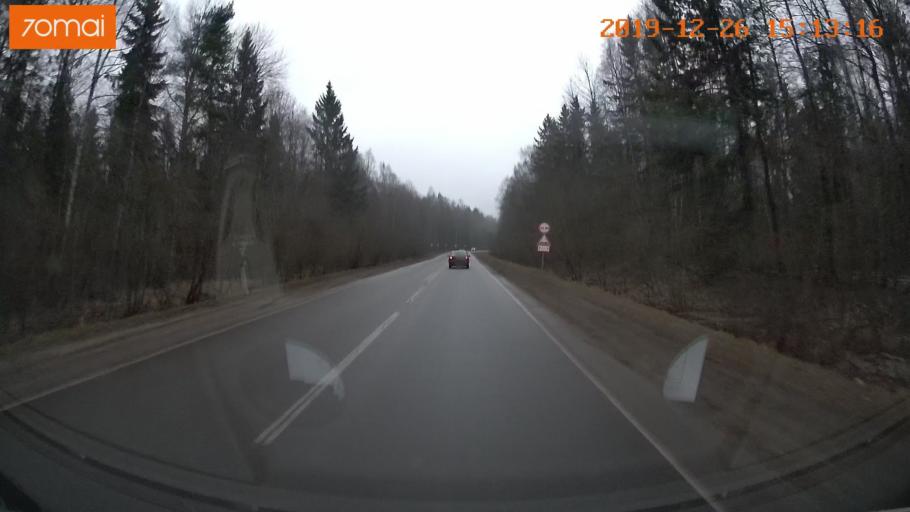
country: RU
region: Jaroslavl
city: Rybinsk
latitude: 58.1188
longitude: 38.8836
